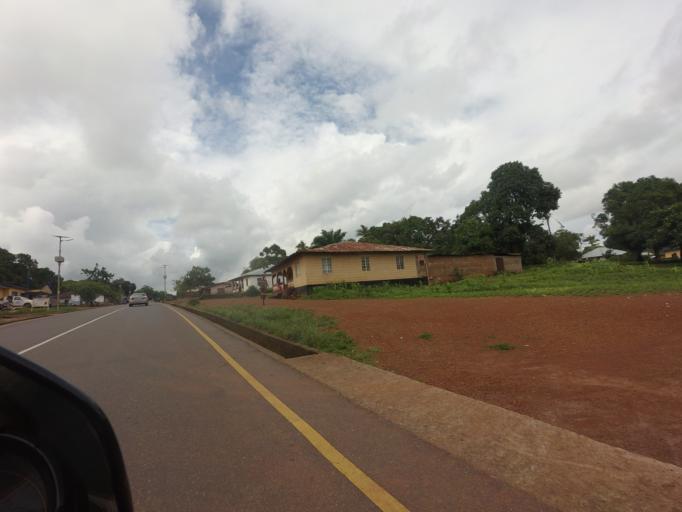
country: SL
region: Northern Province
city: Kambia
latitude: 9.1200
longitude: -12.9184
